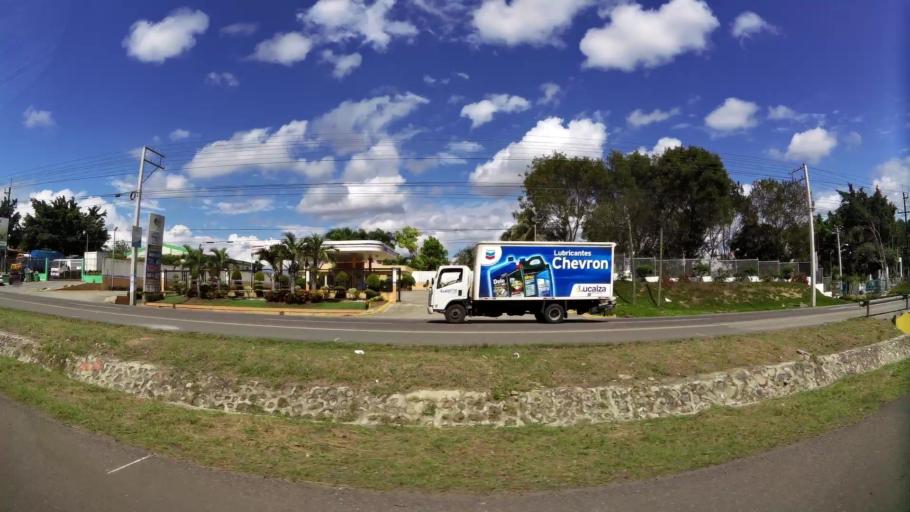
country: DO
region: La Vega
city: Rio Verde Arriba
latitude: 19.3298
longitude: -70.5927
